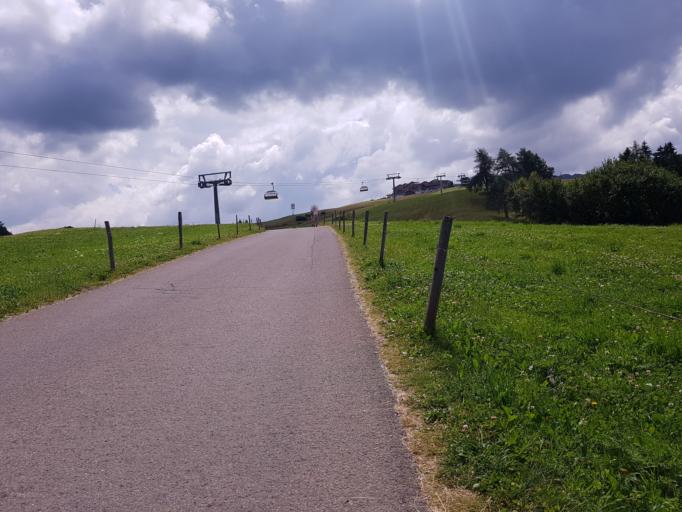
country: IT
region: Trentino-Alto Adige
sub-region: Bolzano
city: Ortisei
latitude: 46.5360
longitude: 11.6235
